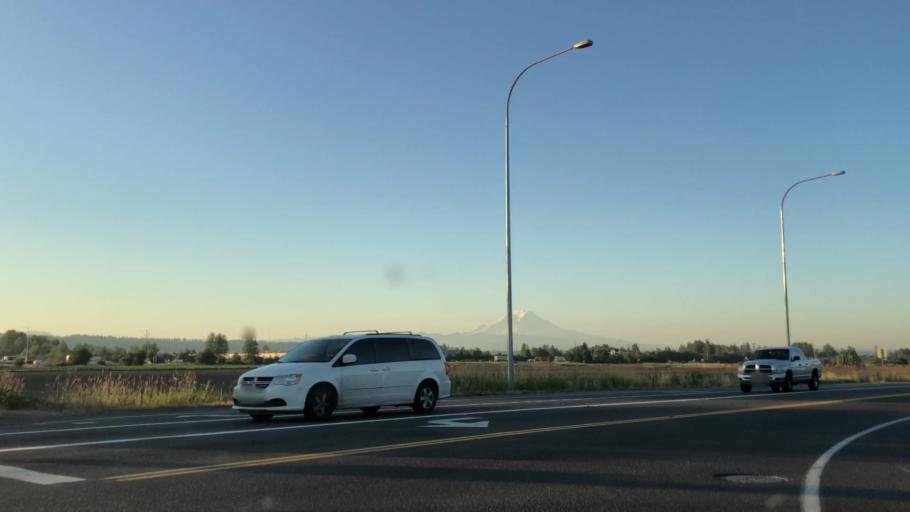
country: US
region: Washington
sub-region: King County
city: Kent
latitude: 47.3535
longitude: -122.2469
